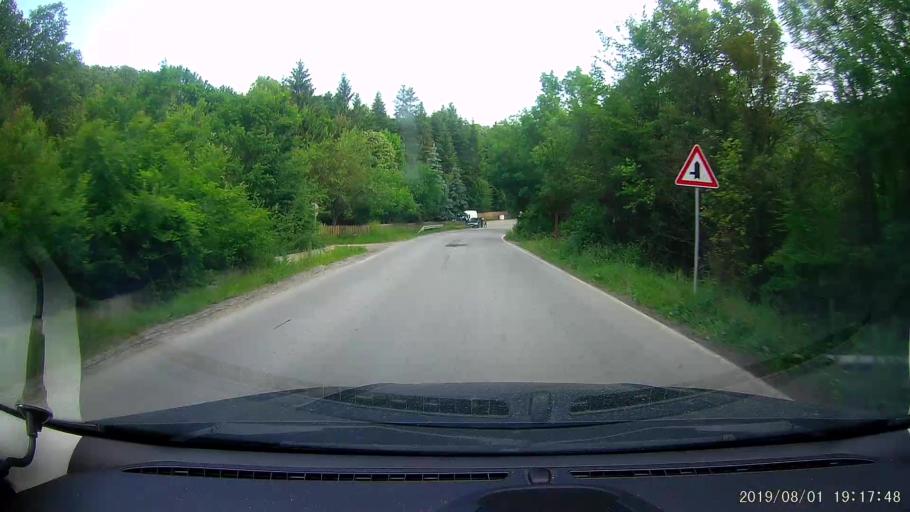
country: BG
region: Shumen
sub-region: Obshtina Smyadovo
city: Smyadovo
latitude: 42.9193
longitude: 26.9394
